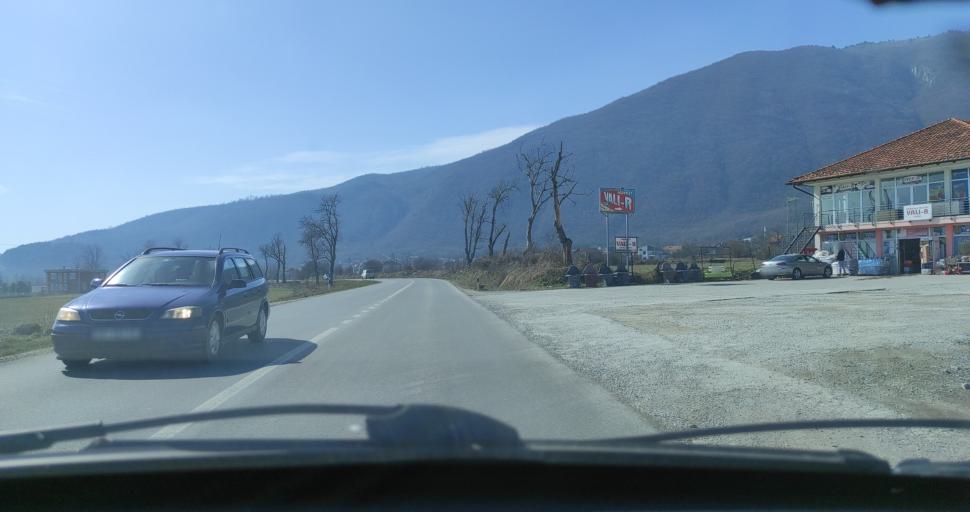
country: XK
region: Gjakova
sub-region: Komuna e Decanit
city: Strellc i Eperm
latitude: 42.6002
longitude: 20.2990
